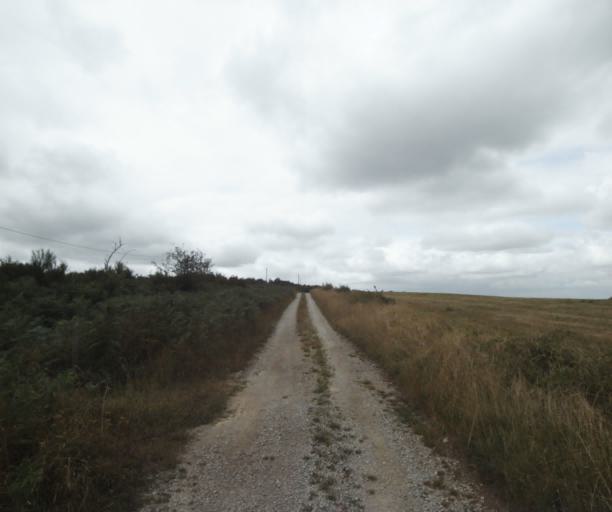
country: FR
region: Midi-Pyrenees
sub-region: Departement du Tarn
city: Soreze
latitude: 43.4322
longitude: 2.1086
